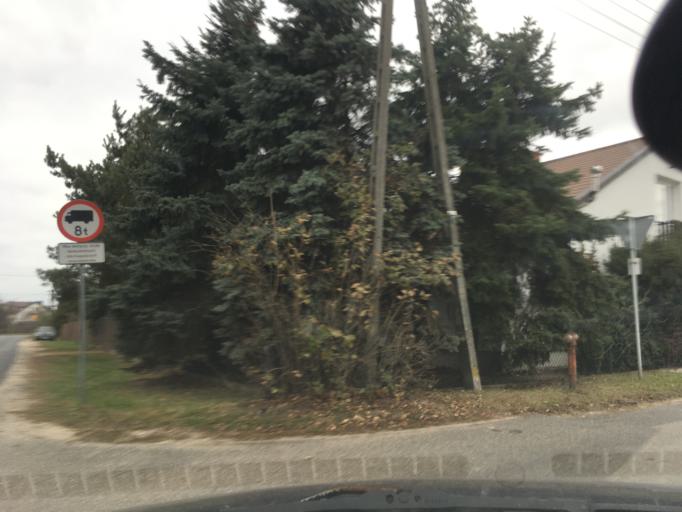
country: PL
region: Lodz Voivodeship
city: Zabia Wola
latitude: 52.0291
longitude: 20.6923
